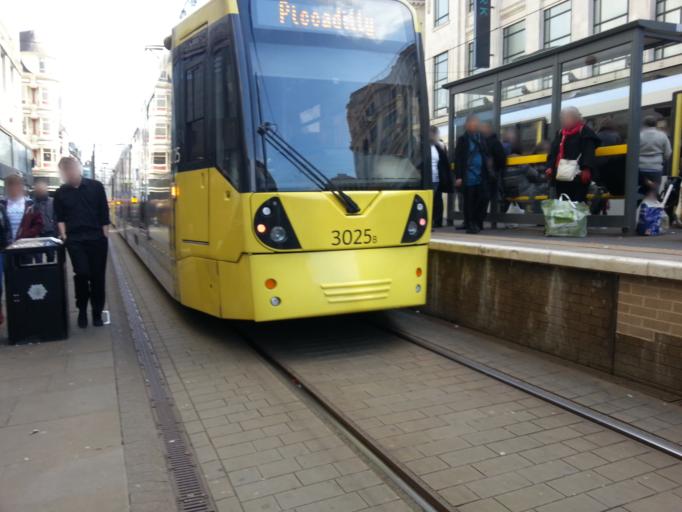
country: GB
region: England
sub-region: Manchester
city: Manchester
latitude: 53.4820
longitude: -2.2393
